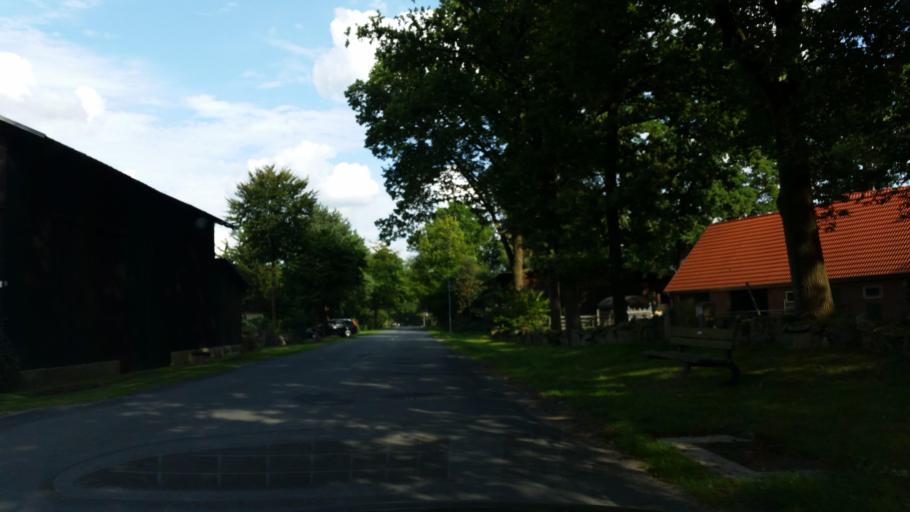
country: DE
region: Lower Saxony
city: Neuenkirchen
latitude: 53.0570
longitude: 9.7407
